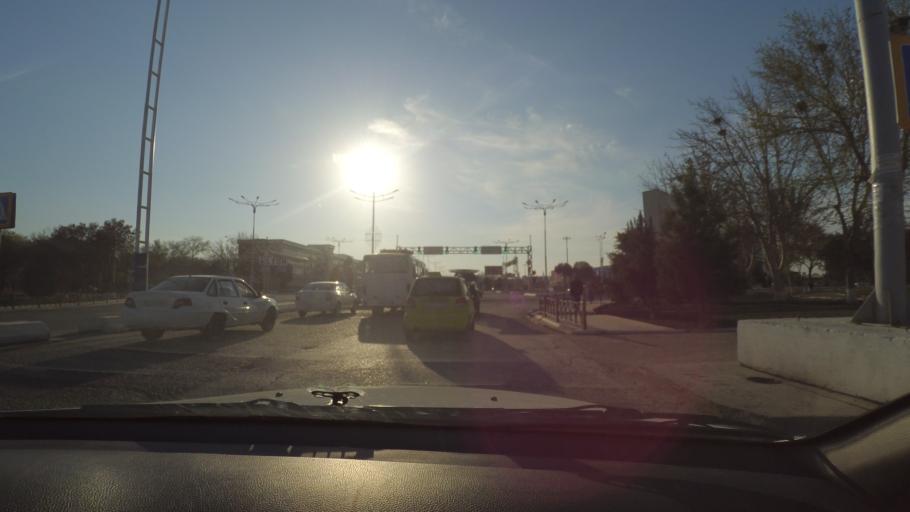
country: UZ
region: Bukhara
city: Bukhara
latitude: 39.7627
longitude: 64.4250
